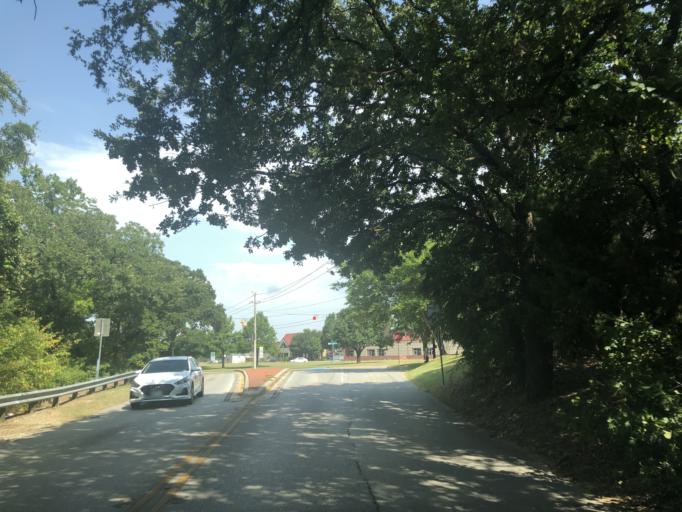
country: US
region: Texas
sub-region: Dallas County
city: Grand Prairie
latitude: 32.7701
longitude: -97.0427
